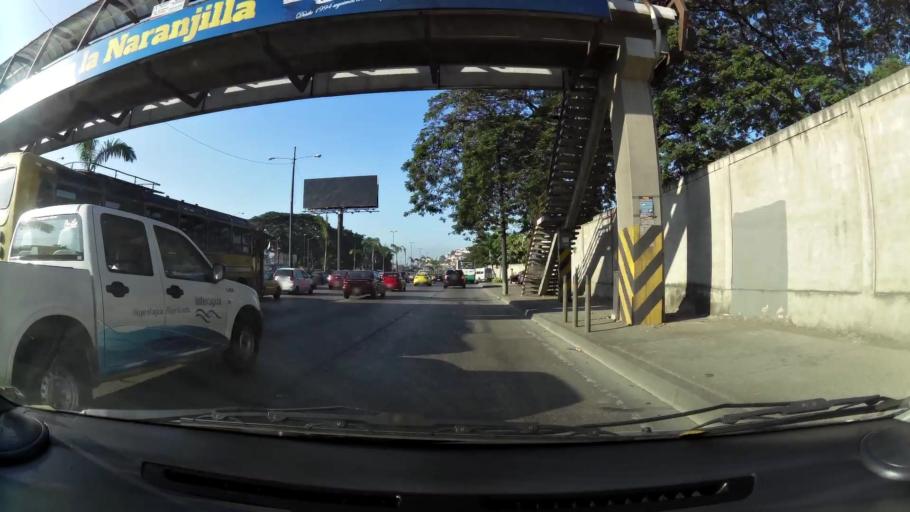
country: EC
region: Guayas
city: Eloy Alfaro
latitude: -2.1658
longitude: -79.8801
